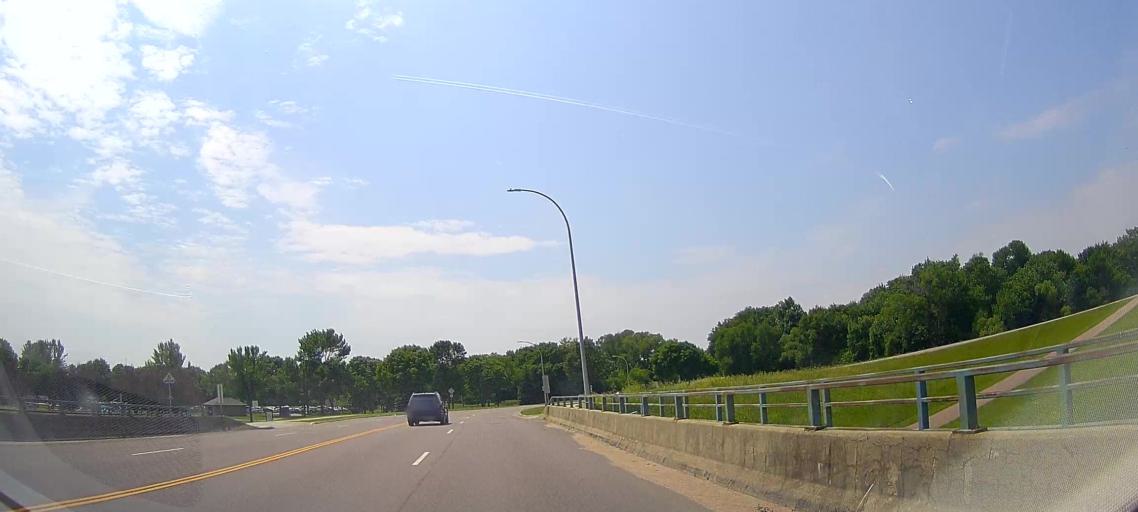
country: US
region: South Dakota
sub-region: Minnehaha County
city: Sioux Falls
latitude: 43.5080
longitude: -96.7601
